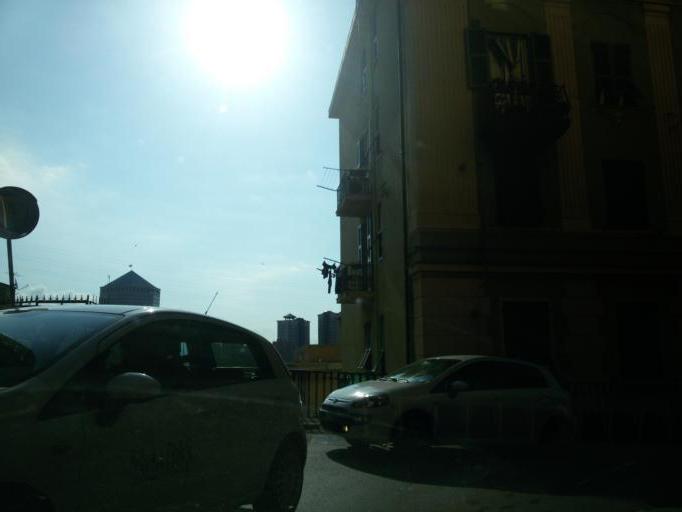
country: IT
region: Liguria
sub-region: Provincia di Genova
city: San Teodoro
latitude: 44.4117
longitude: 8.8994
